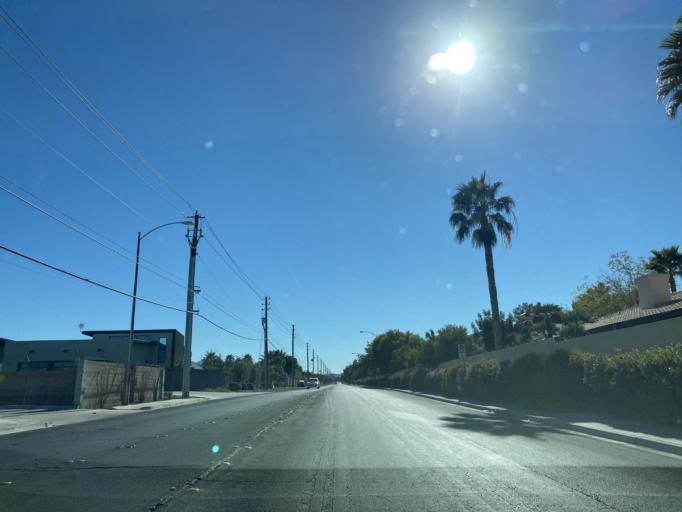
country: US
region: Nevada
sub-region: Clark County
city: Whitney
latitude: 36.0851
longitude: -115.0868
